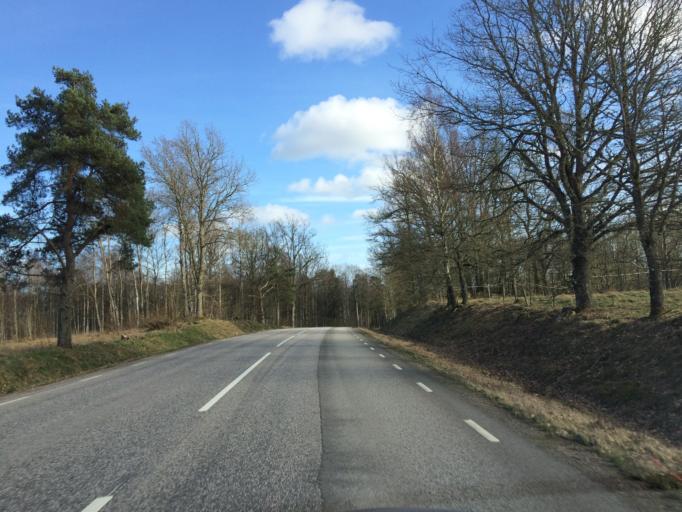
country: SE
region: Kronoberg
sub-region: Almhults Kommun
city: AElmhult
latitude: 56.5741
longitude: 14.1129
